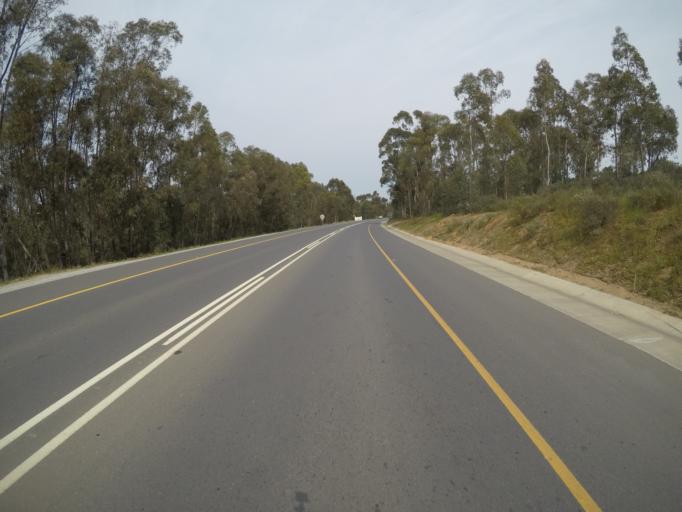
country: ZA
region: Western Cape
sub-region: West Coast District Municipality
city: Malmesbury
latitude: -33.4606
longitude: 18.7449
